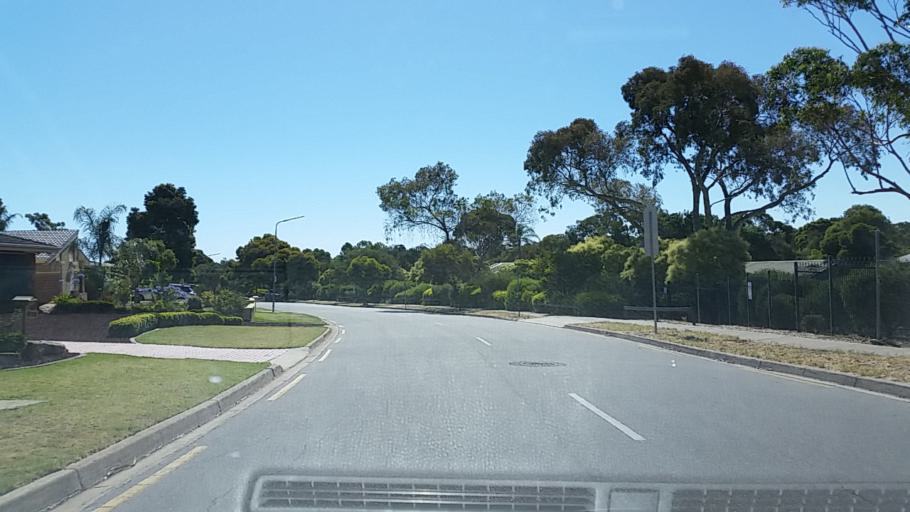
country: AU
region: South Australia
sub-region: Tea Tree Gully
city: Hope Valley
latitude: -34.8024
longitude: 138.7012
